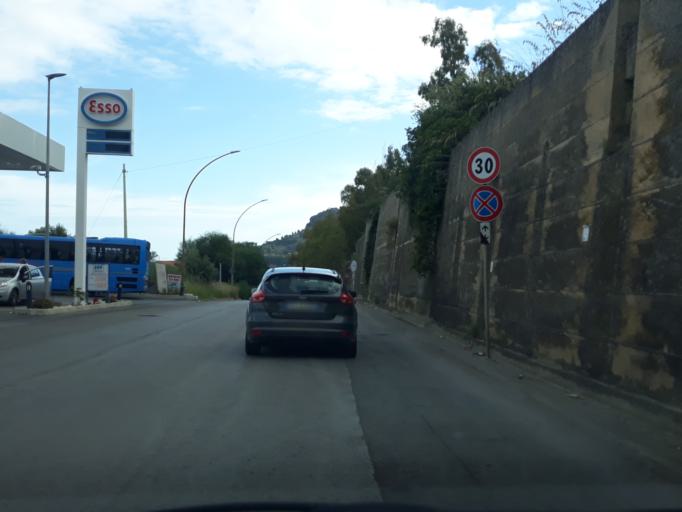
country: IT
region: Sicily
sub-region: Palermo
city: Cefalu
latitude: 38.0267
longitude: 14.0157
